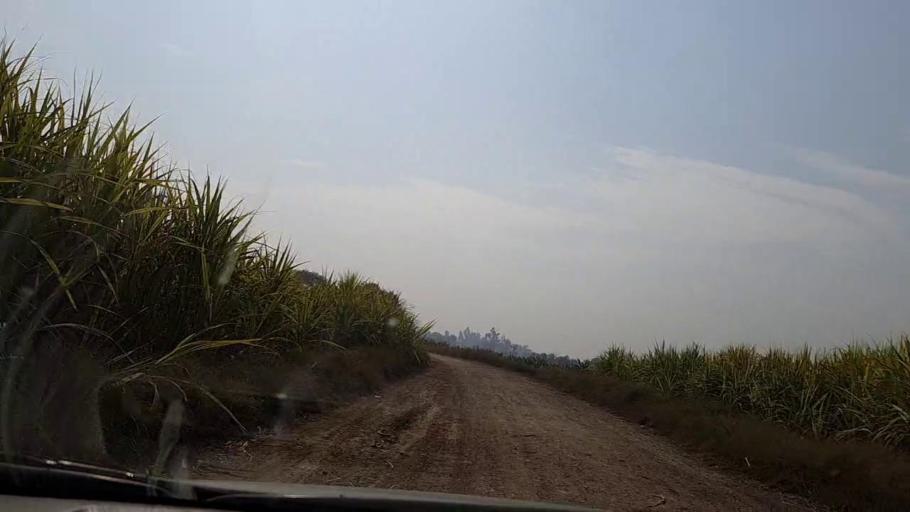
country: PK
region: Sindh
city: Daulatpur
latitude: 26.5371
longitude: 67.9868
